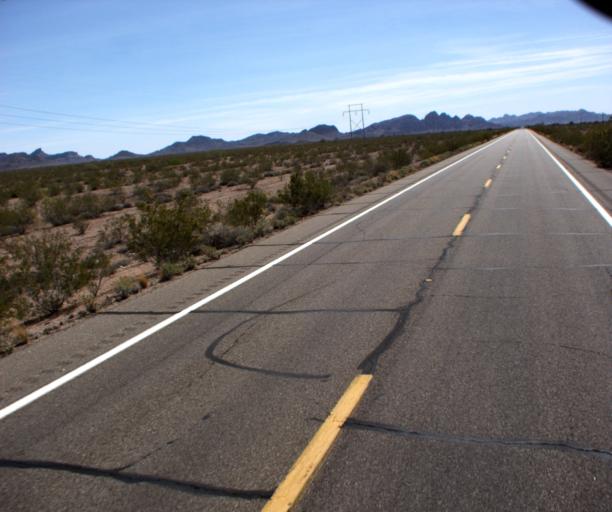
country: US
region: Arizona
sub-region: La Paz County
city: Quartzsite
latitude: 33.3633
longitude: -114.2171
